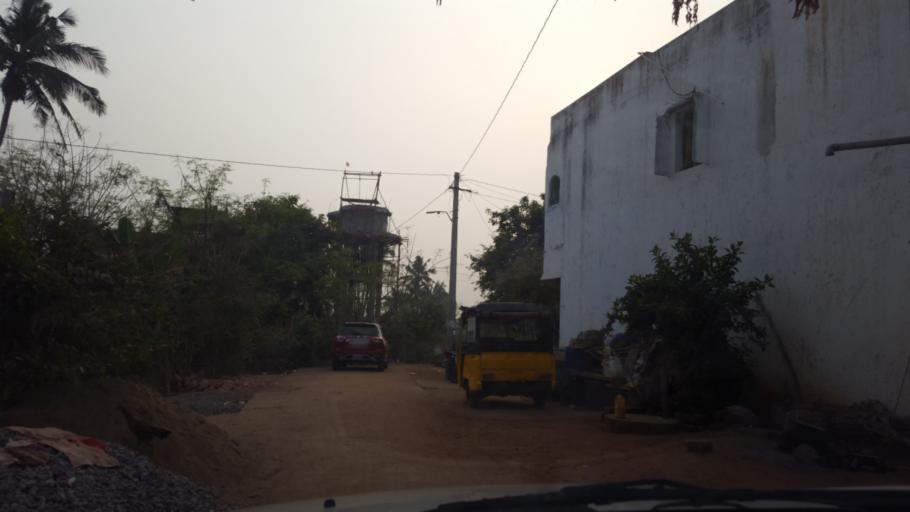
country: IN
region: Andhra Pradesh
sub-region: Srikakulam
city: Palasa
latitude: 18.7604
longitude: 84.5119
